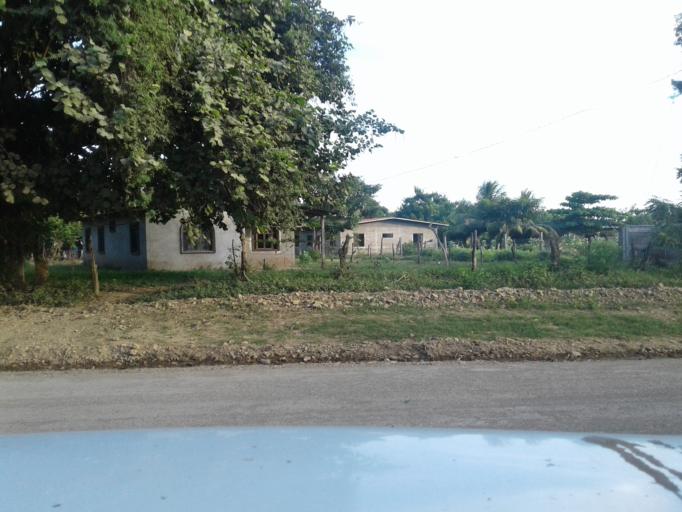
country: NI
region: Rivas
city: Tola
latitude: 11.4813
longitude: -86.0996
